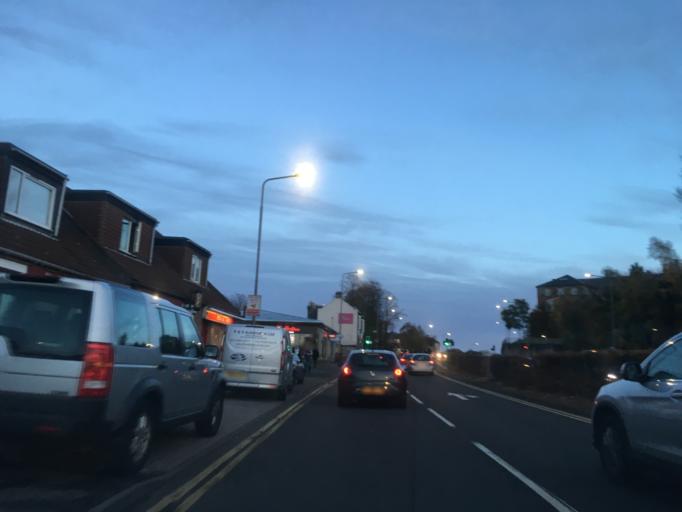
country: GB
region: Scotland
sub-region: Fife
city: Dunfermline
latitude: 56.0618
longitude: -3.4462
